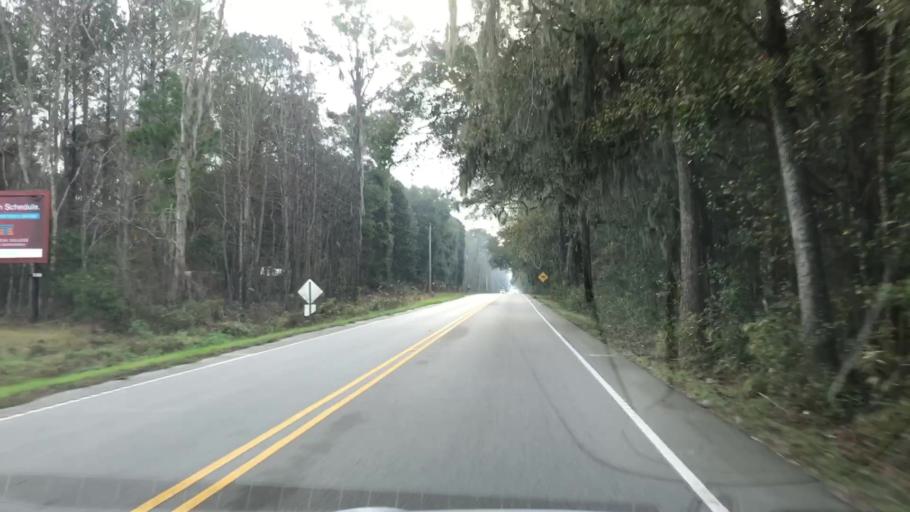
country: US
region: South Carolina
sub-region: Jasper County
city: Ridgeland
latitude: 32.5389
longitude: -80.9106
